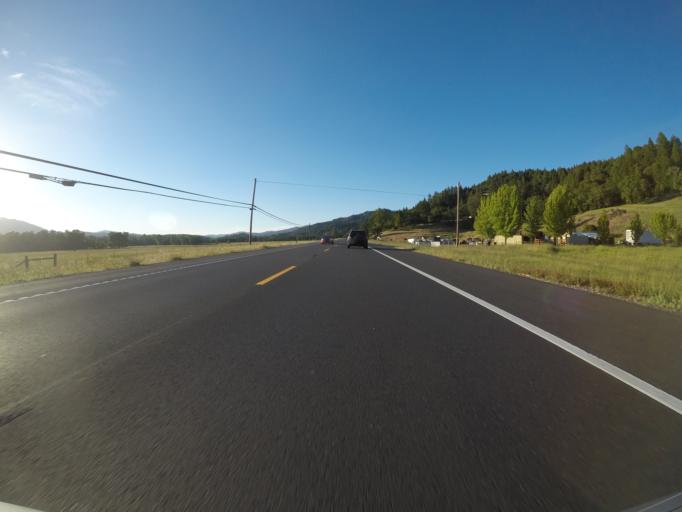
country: US
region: California
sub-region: Mendocino County
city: Laytonville
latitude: 39.6681
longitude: -123.4761
